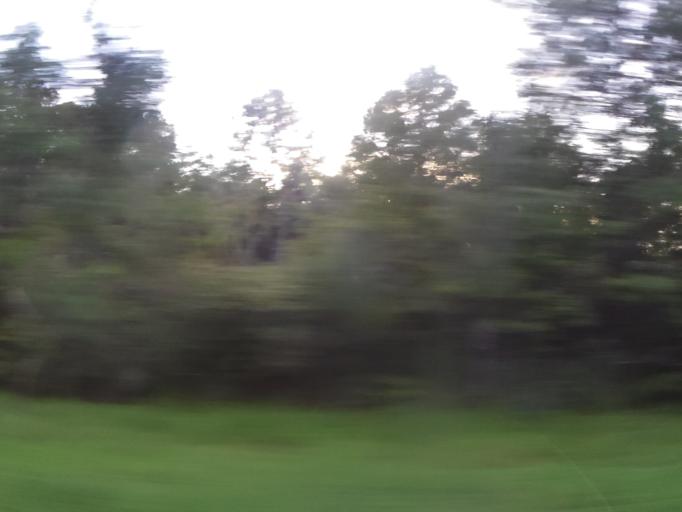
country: US
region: Georgia
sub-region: Camden County
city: Woodbine
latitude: 30.9821
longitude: -81.7278
